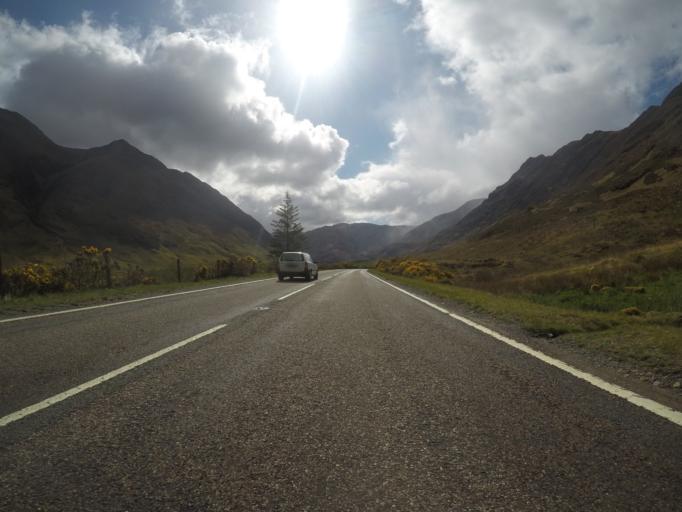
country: GB
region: Scotland
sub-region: Highland
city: Fort William
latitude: 57.1949
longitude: -5.3887
